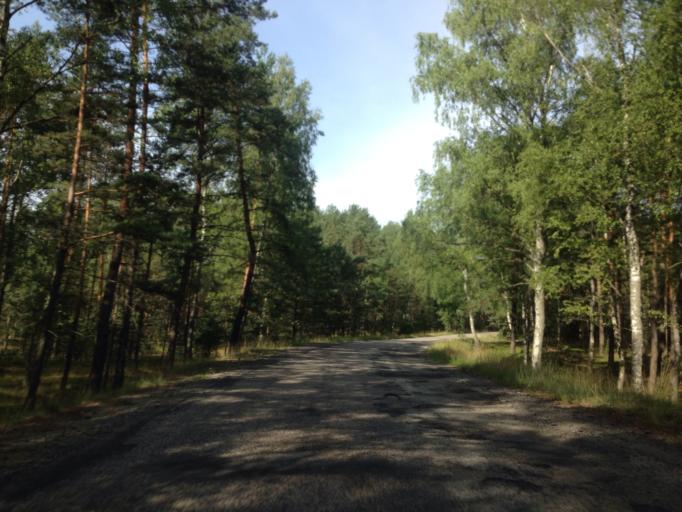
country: PL
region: Kujawsko-Pomorskie
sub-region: Powiat swiecki
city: Osie
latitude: 53.6985
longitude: 18.3069
